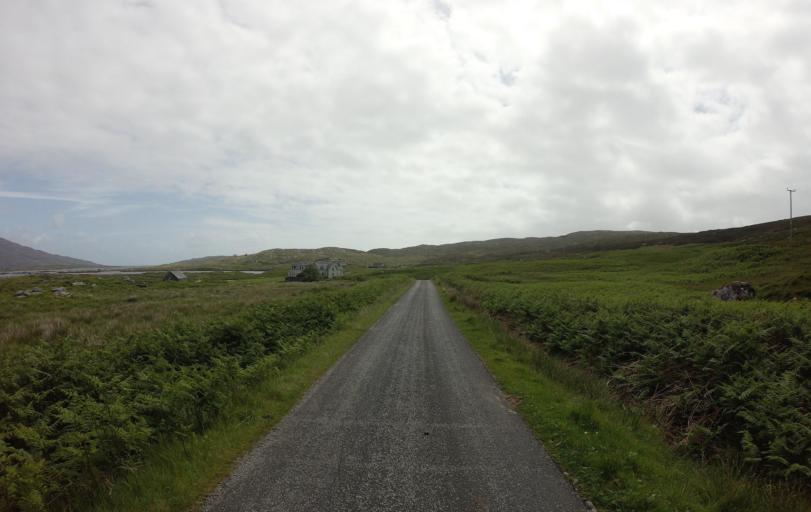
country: GB
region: Scotland
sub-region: Eilean Siar
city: Isle of South Uist
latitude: 57.1372
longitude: -7.3407
